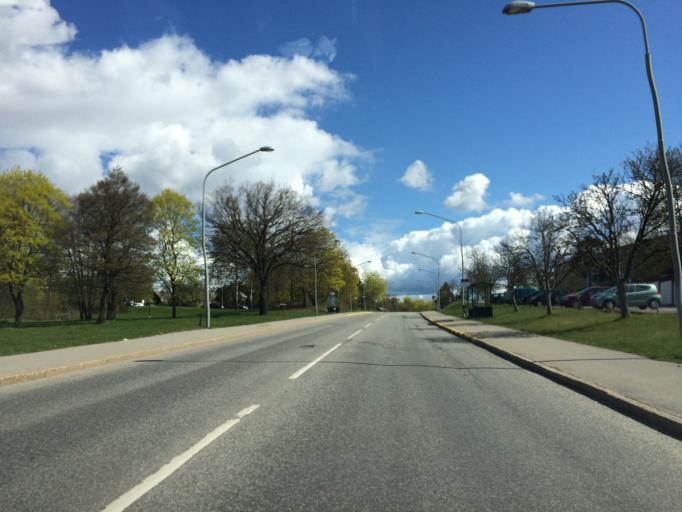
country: SE
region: Stockholm
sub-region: Huddinge Kommun
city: Segeltorp
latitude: 59.2881
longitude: 17.9132
